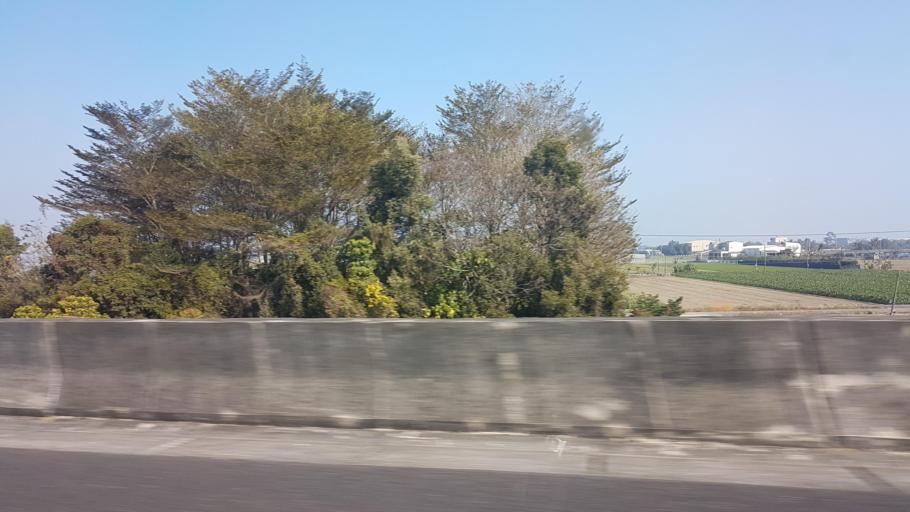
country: TW
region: Taiwan
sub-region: Chiayi
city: Taibao
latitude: 23.4195
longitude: 120.3820
